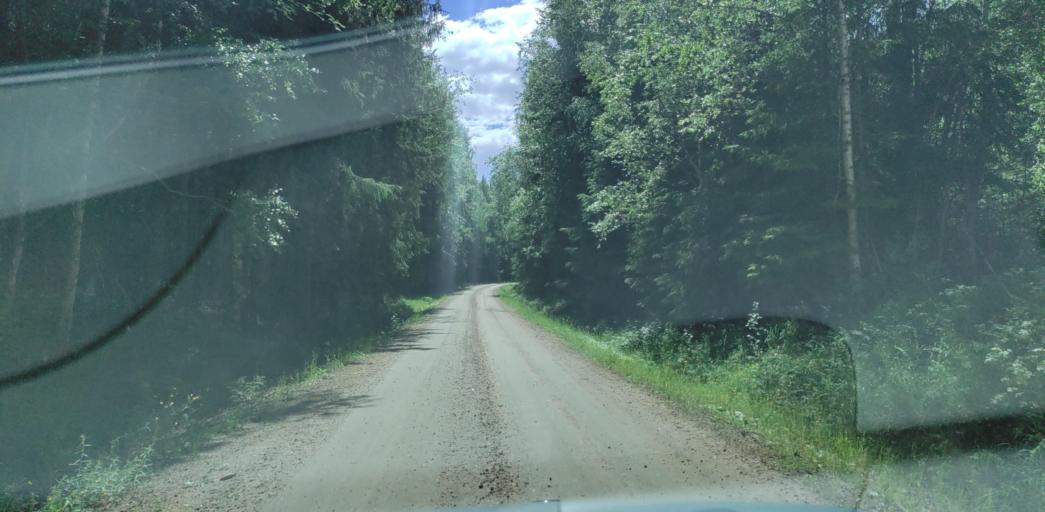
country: SE
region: Vaermland
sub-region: Sunne Kommun
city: Sunne
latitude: 60.0451
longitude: 13.2560
